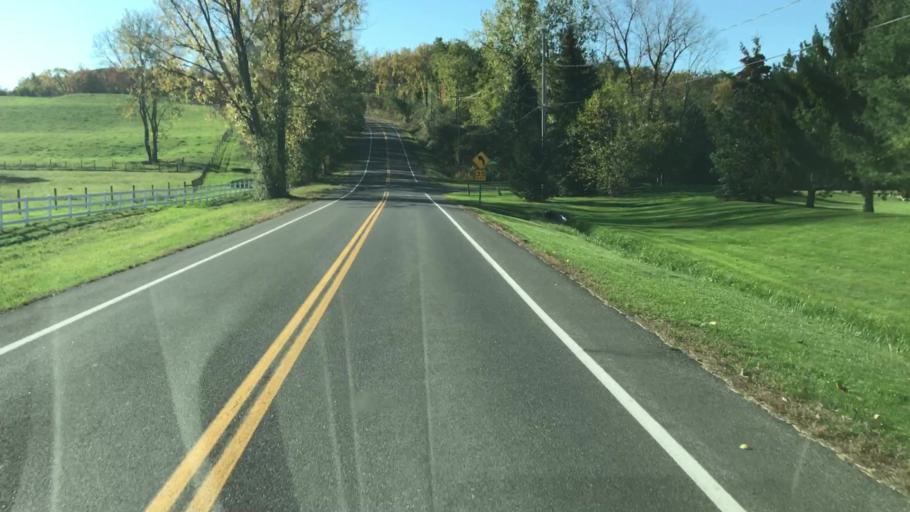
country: US
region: New York
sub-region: Onondaga County
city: Fayetteville
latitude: 42.9892
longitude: -76.0450
